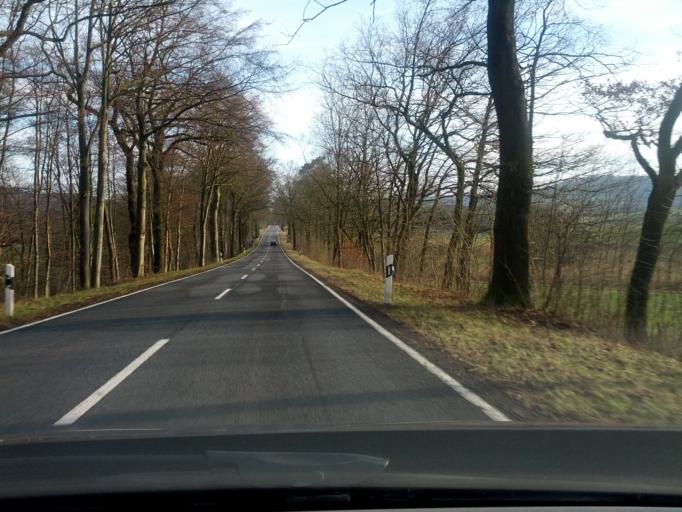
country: DE
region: Hesse
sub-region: Regierungsbezirk Kassel
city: Weissenborn
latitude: 51.0820
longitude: 10.1413
